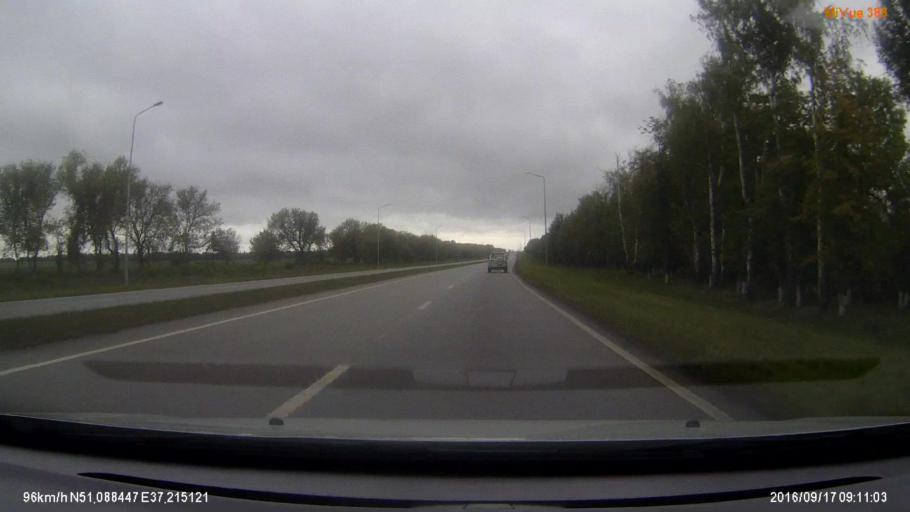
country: RU
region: Belgorod
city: Skorodnoye
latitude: 51.0882
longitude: 37.2150
